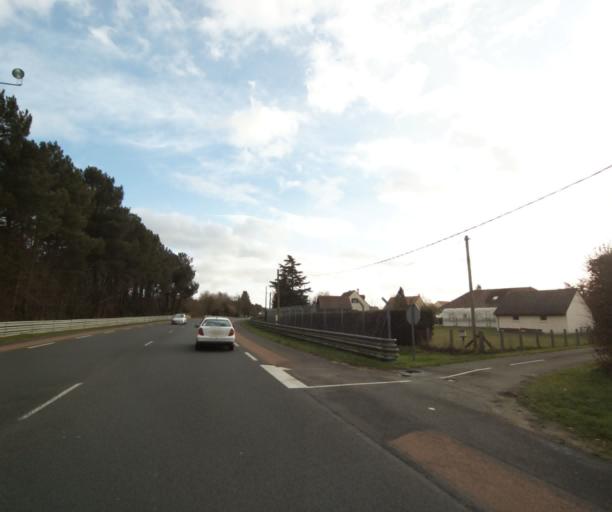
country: FR
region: Pays de la Loire
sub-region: Departement de la Sarthe
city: Arnage
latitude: 47.9271
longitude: 0.2132
